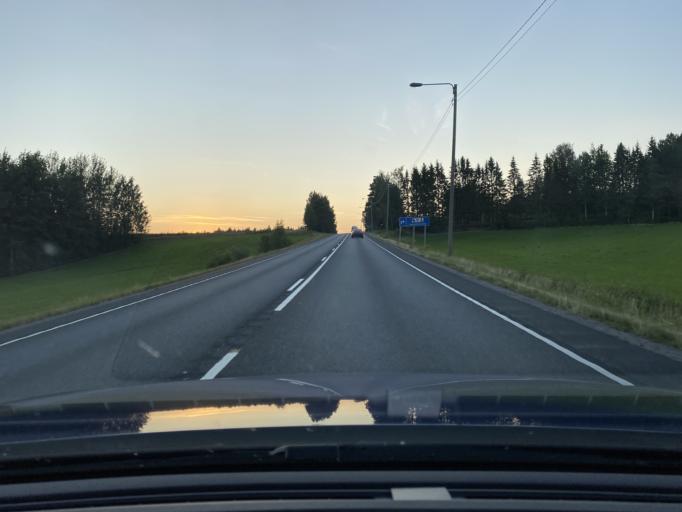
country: FI
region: Pirkanmaa
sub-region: Luoteis-Pirkanmaa
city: Ikaalinen
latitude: 61.7693
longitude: 23.0149
